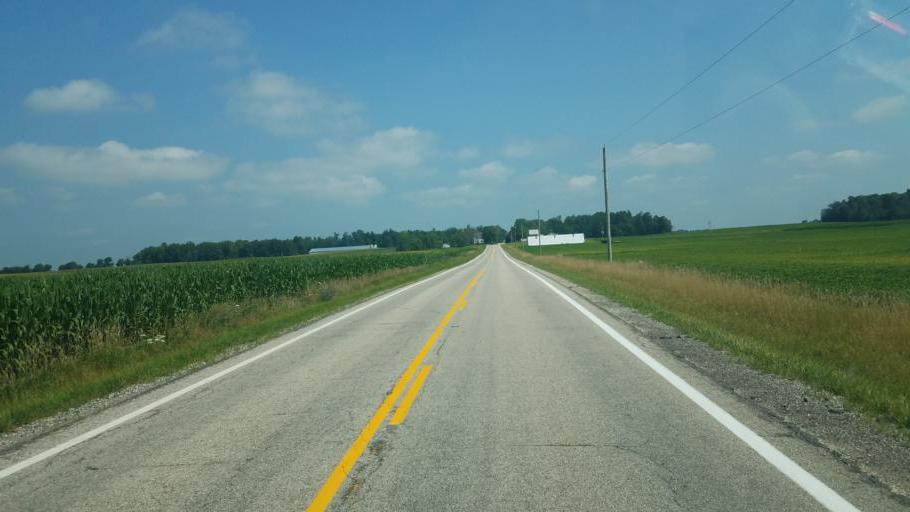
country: US
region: Ohio
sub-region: Crawford County
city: Bucyrus
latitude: 40.8530
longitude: -82.8556
